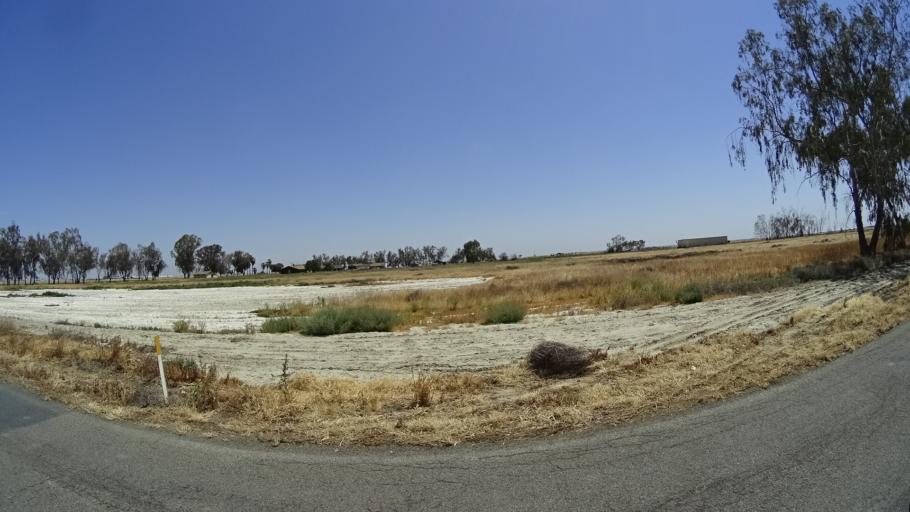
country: US
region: California
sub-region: Kings County
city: Armona
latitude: 36.2097
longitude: -119.7086
